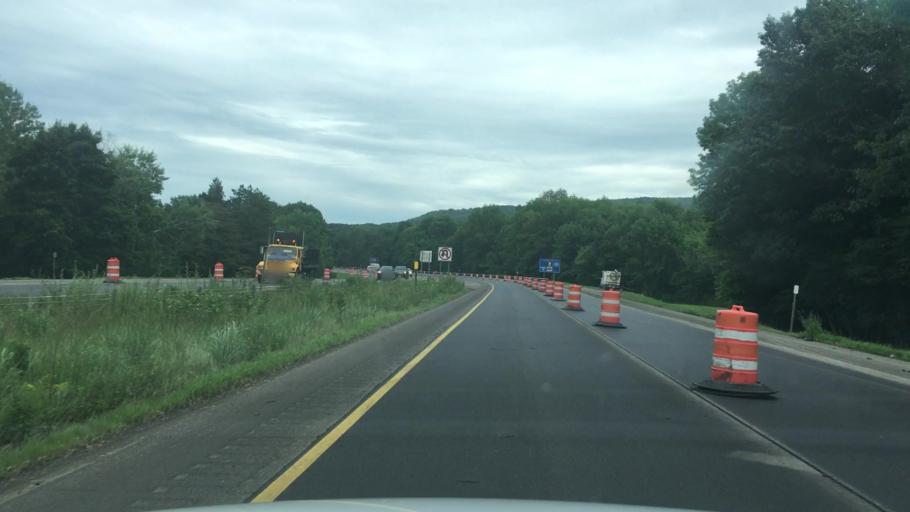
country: US
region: New York
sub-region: Otsego County
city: Oneonta
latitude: 42.4414
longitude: -75.0772
